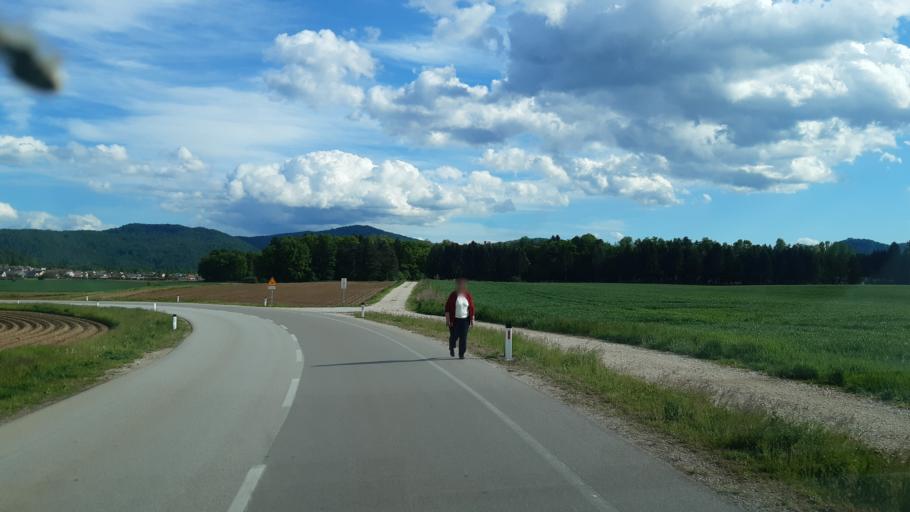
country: SI
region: Vodice
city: Vodice
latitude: 46.1837
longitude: 14.4968
